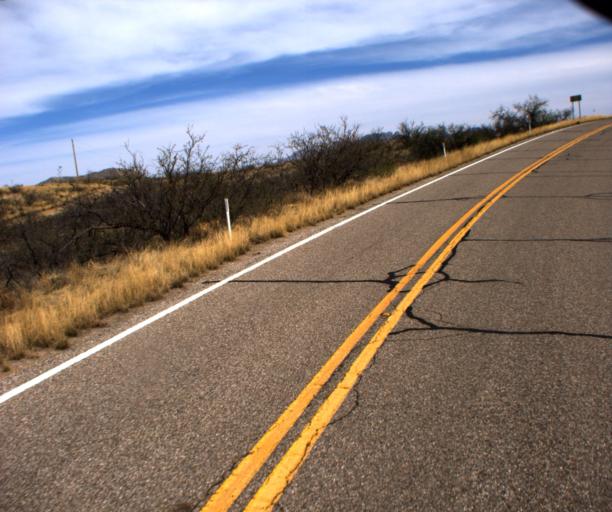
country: US
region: Arizona
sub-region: Cochise County
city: Willcox
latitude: 32.1593
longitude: -109.5669
